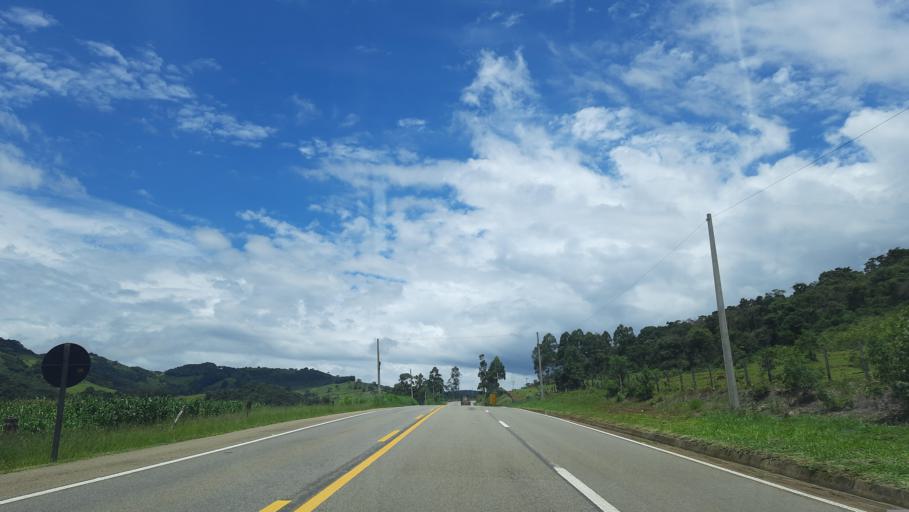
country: BR
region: Sao Paulo
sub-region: Vargem Grande Do Sul
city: Vargem Grande do Sul
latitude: -21.8285
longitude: -46.7704
